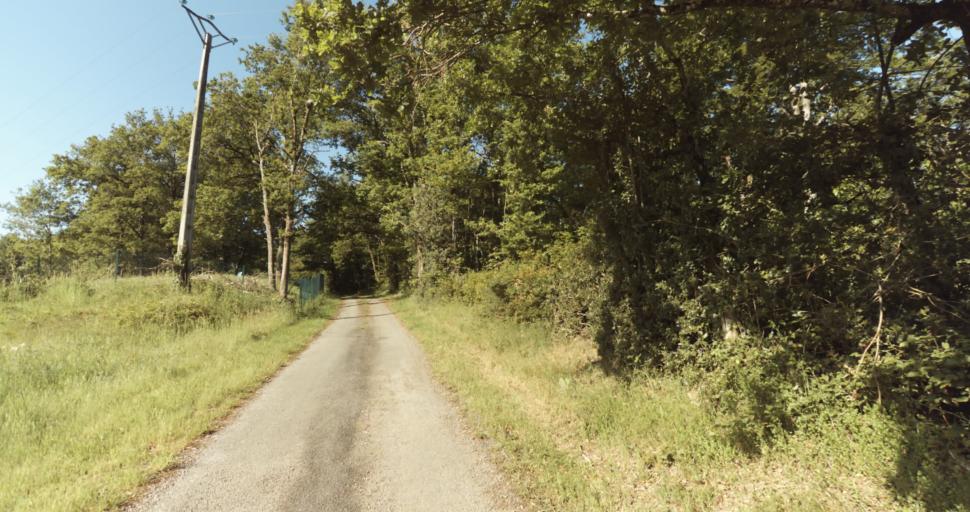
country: FR
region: Limousin
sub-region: Departement de la Haute-Vienne
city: Solignac
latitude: 45.7326
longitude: 1.2398
